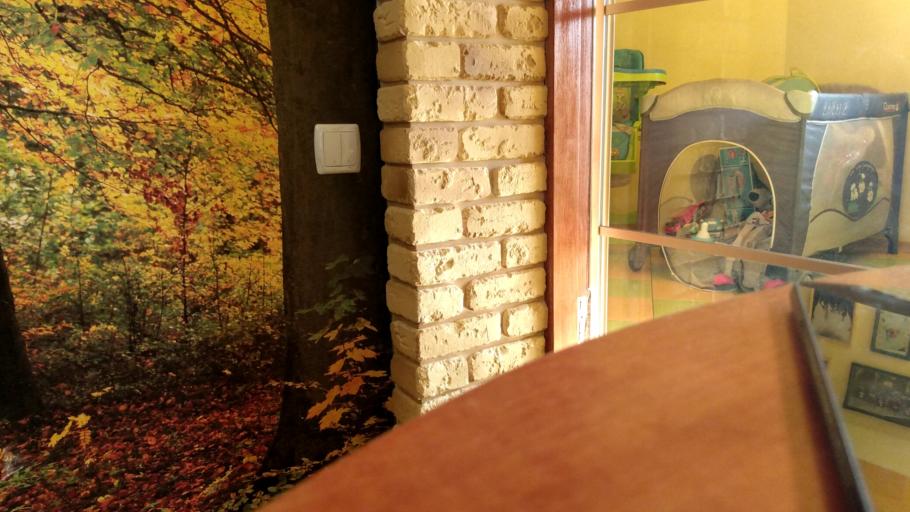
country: RU
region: Tverskaya
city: Radchenko
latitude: 56.6971
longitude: 36.4257
